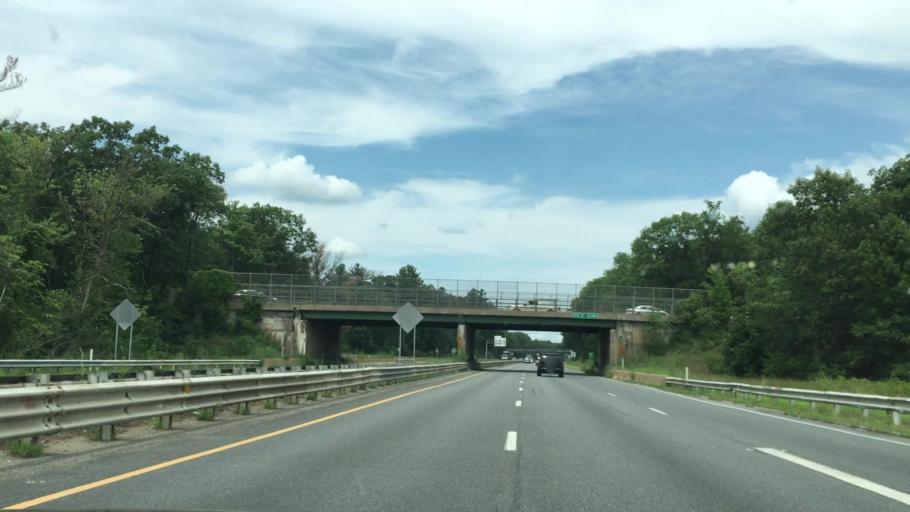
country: US
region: Massachusetts
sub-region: Middlesex County
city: Acton
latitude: 42.4773
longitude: -71.4479
